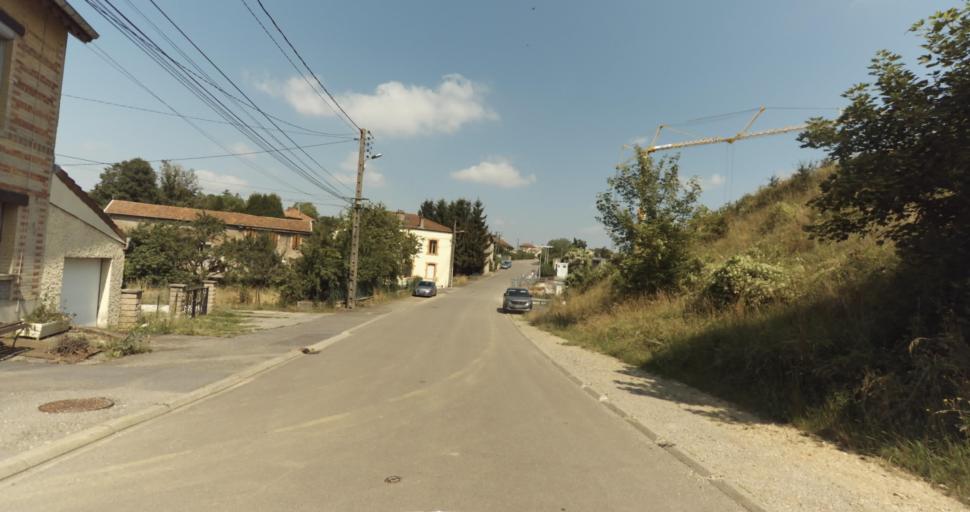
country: FR
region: Lorraine
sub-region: Departement de Meurthe-et-Moselle
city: Mancieulles
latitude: 49.2813
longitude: 5.8962
